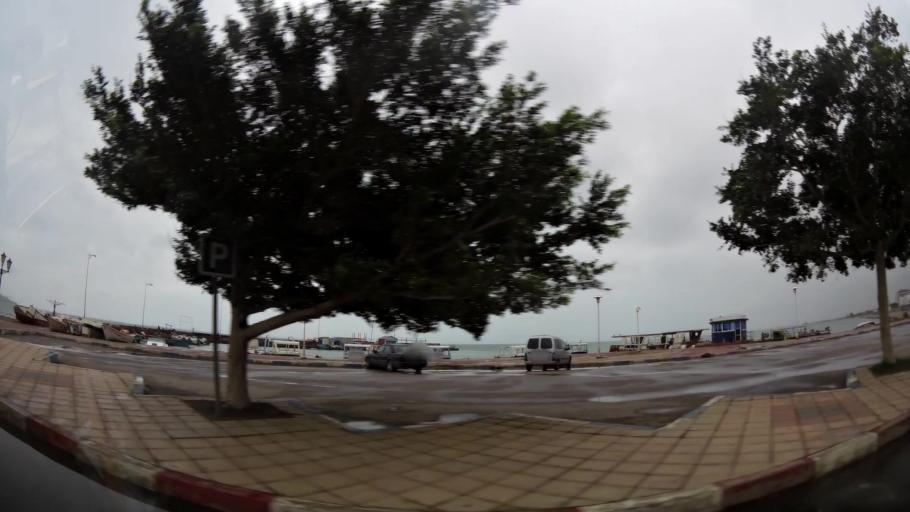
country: MA
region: Oriental
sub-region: Nador
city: Nador
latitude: 35.1855
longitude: -2.9249
